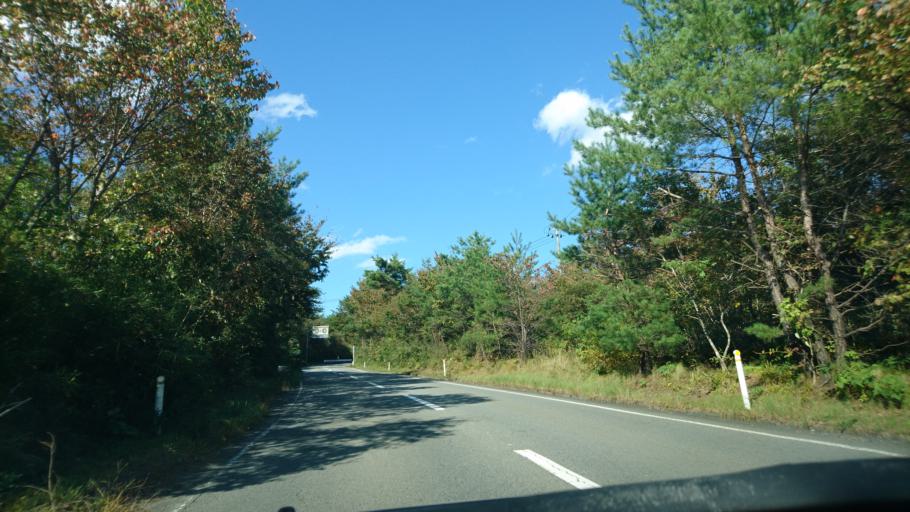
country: JP
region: Iwate
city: Ichinoseki
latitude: 38.8506
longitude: 141.0362
